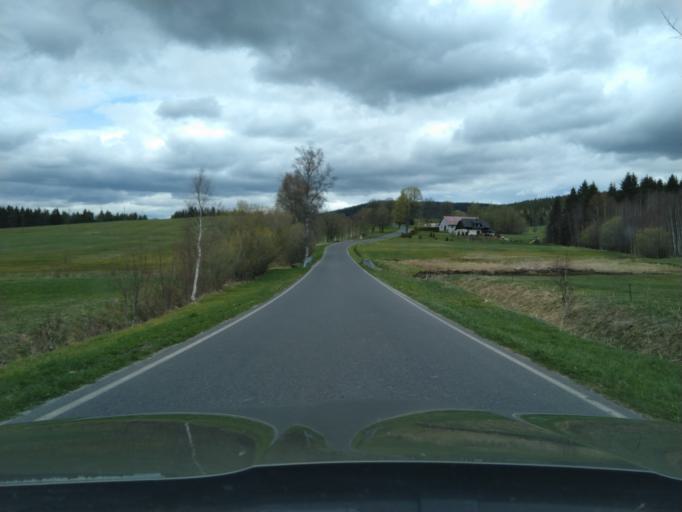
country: CZ
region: Jihocesky
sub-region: Okres Prachatice
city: Borova Lada
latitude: 48.9970
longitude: 13.6692
